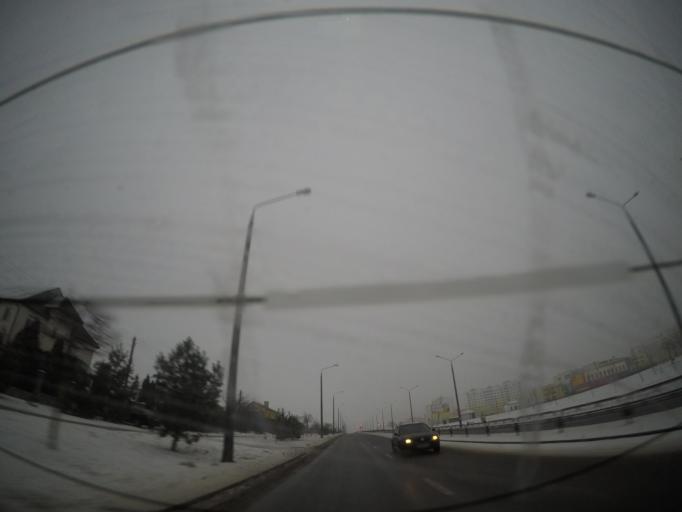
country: BY
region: Grodnenskaya
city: Hrodna
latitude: 53.6264
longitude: 23.8055
